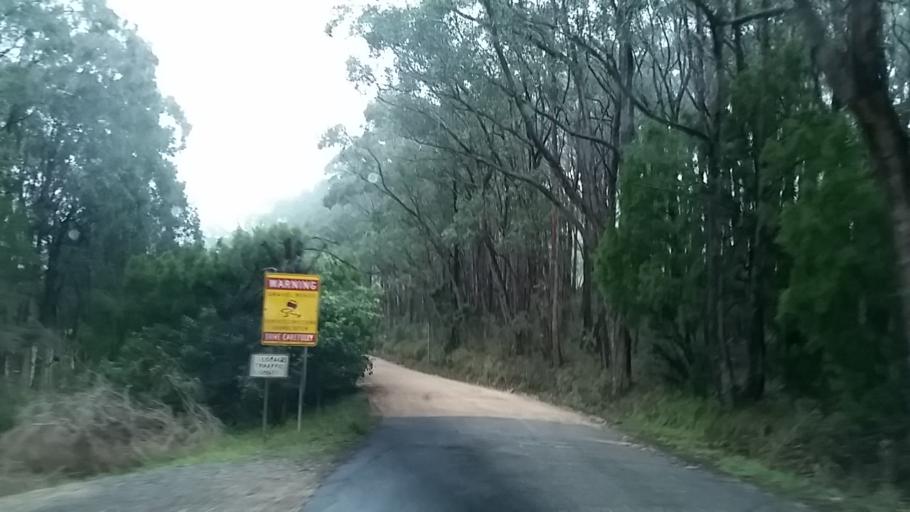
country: AU
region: South Australia
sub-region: Adelaide Hills
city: Adelaide Hills
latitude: -34.9299
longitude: 138.7461
